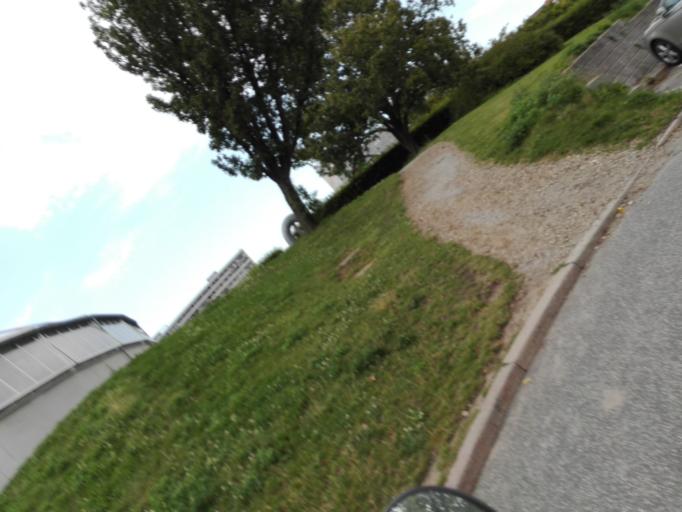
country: DK
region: Central Jutland
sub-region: Arhus Kommune
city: Arhus
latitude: 56.1595
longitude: 10.1941
